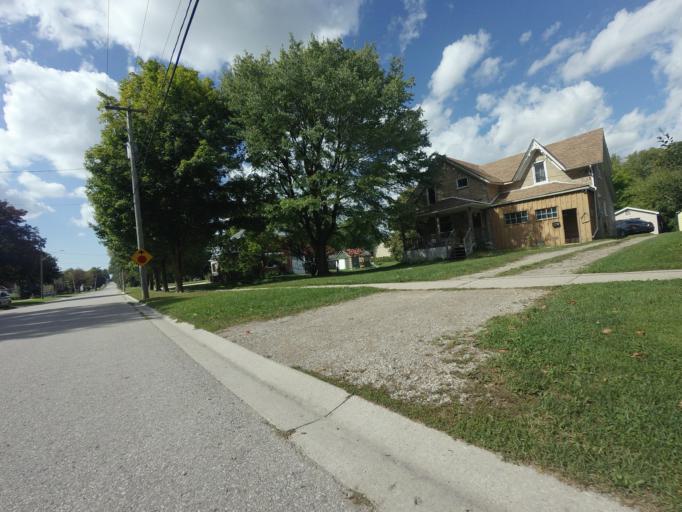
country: CA
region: Ontario
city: Huron East
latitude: 43.7342
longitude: -81.4241
